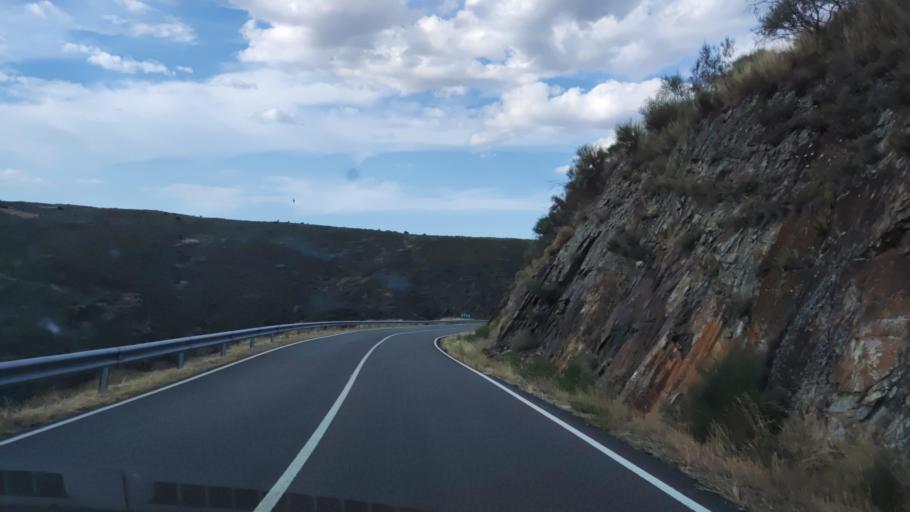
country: ES
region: Castille and Leon
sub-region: Provincia de Salamanca
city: Pastores
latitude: 40.4959
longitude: -6.4948
